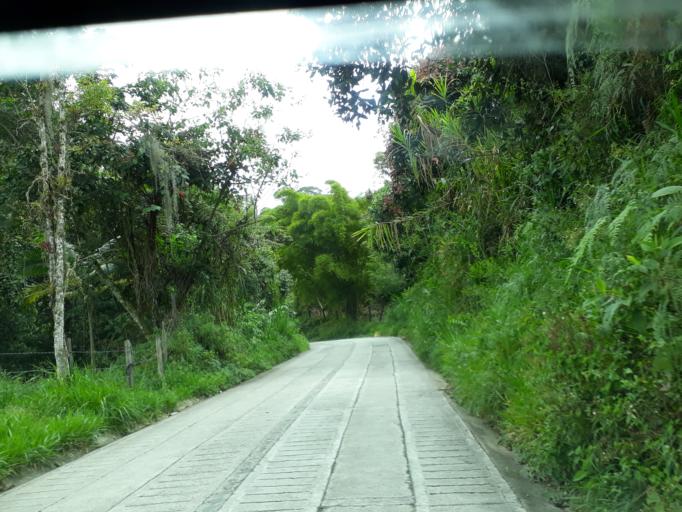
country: CO
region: Cundinamarca
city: Topaipi
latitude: 5.2669
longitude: -74.1934
